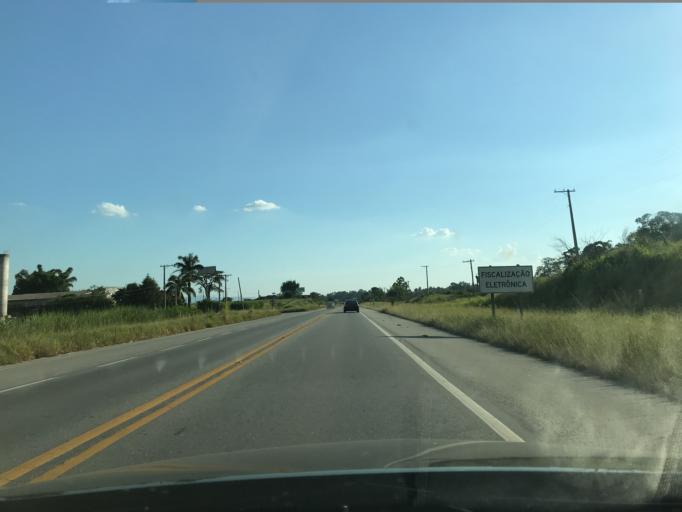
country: BR
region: Sao Paulo
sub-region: Tremembe
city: Tremembe
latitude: -22.9714
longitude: -45.6434
